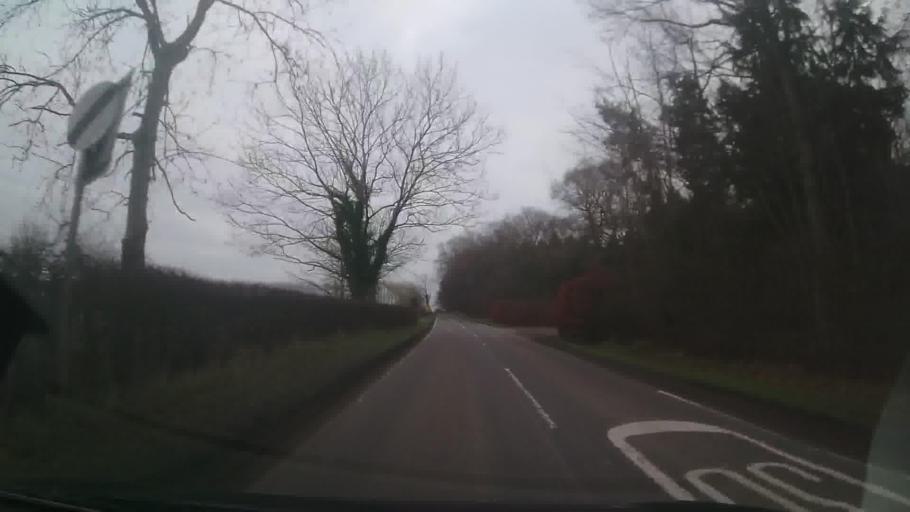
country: GB
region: England
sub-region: Shropshire
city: Bicton
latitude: 52.7795
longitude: -2.8344
